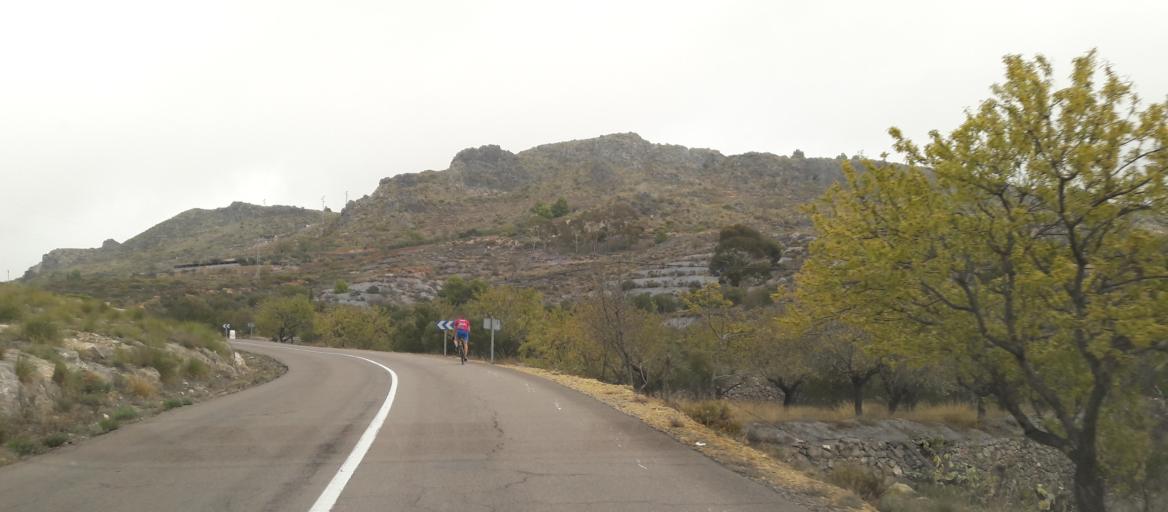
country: ES
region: Andalusia
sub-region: Provincia de Almeria
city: Enix
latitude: 36.8786
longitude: -2.6230
